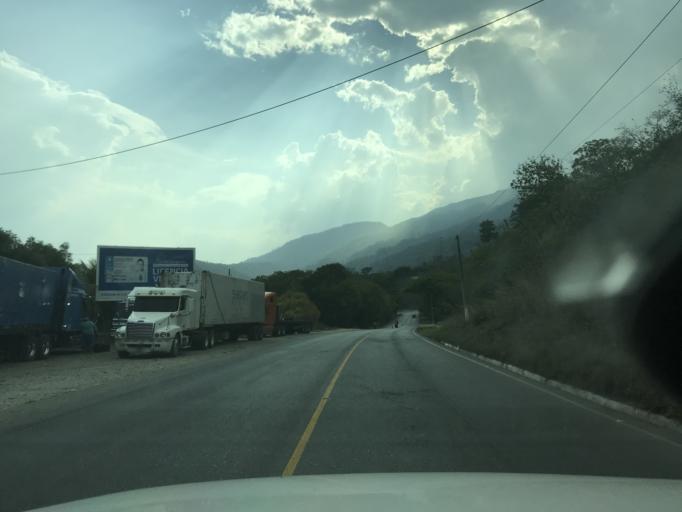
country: GT
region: Zacapa
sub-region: Municipio de Zacapa
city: Gualan
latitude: 15.1820
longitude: -89.2983
